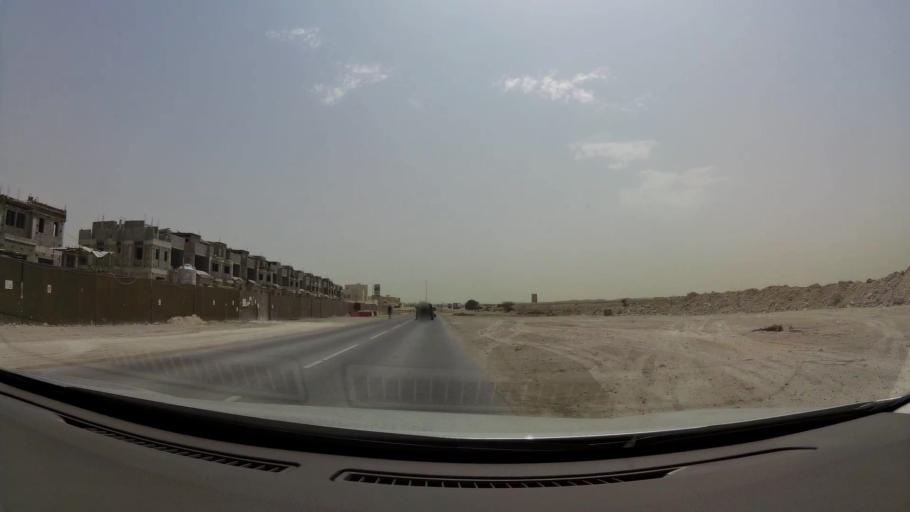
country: QA
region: Baladiyat ar Rayyan
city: Ar Rayyan
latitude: 25.2300
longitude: 51.4093
